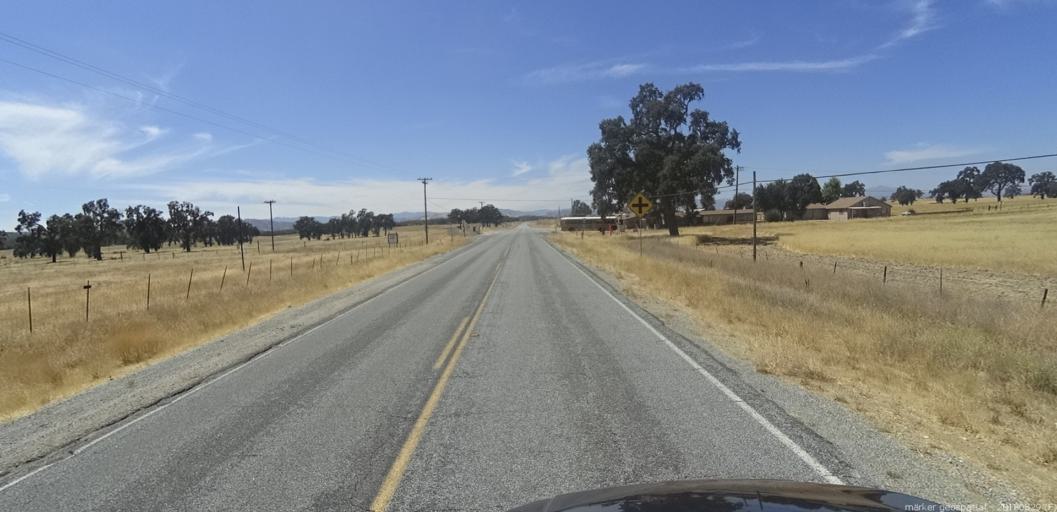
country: US
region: California
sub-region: Monterey County
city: King City
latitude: 35.9368
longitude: -121.0810
